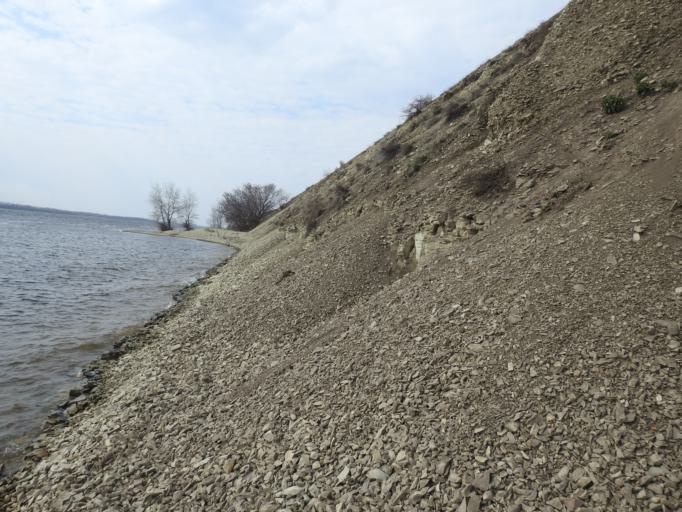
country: RU
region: Saratov
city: Voskresenskoye
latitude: 51.8058
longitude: 46.9147
